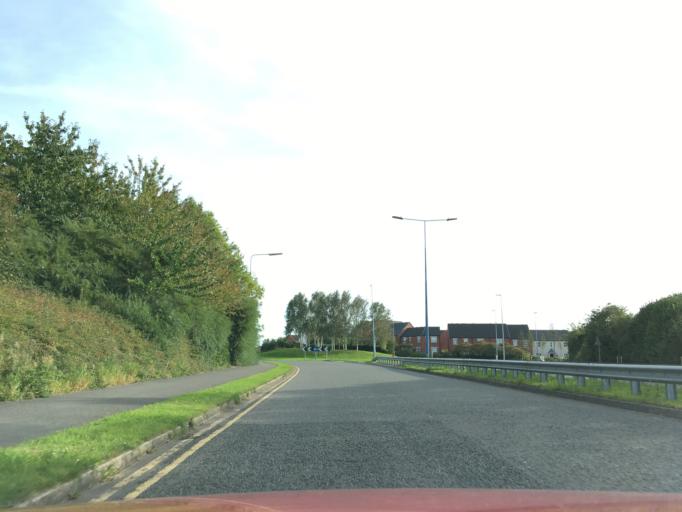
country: GB
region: England
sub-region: South Gloucestershire
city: Stoke Gifford
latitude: 51.5182
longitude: -2.5305
